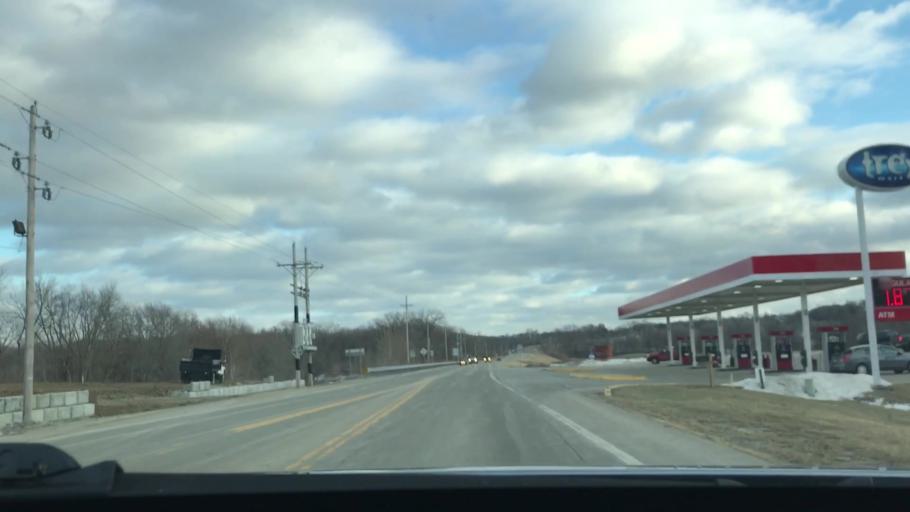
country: US
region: Missouri
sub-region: Platte County
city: Platte City
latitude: 39.3754
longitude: -94.7928
